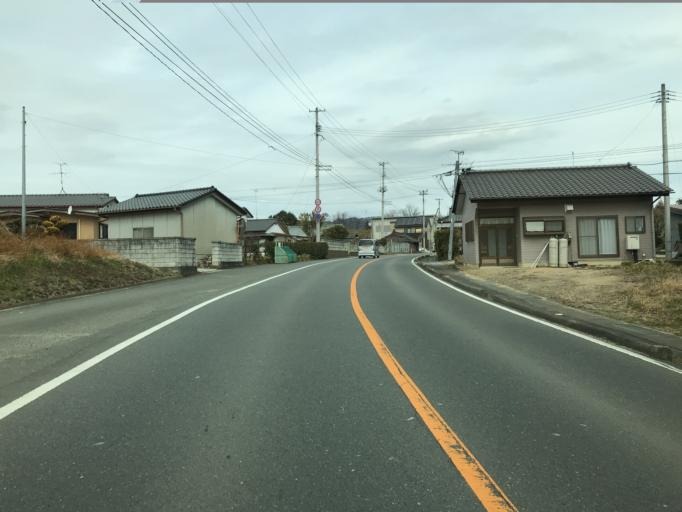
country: JP
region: Fukushima
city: Iwaki
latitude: 37.0973
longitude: 140.8736
